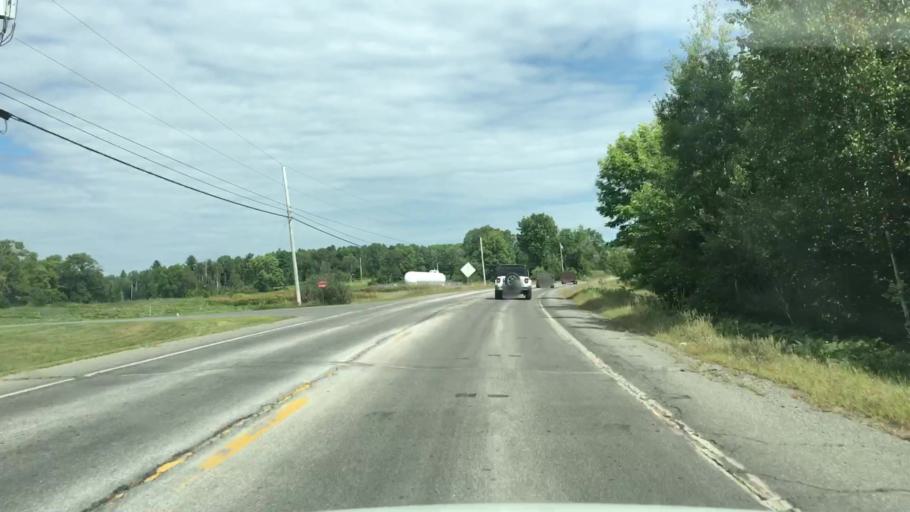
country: US
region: Maine
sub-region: Piscataquis County
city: Dover-Foxcroft
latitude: 45.1538
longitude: -69.2358
